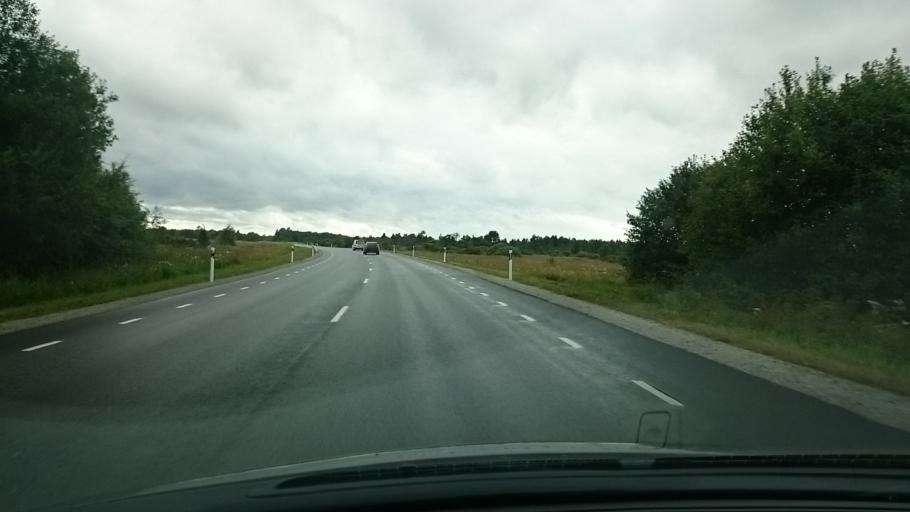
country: EE
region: Harju
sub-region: Keila linn
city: Keila
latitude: 59.3043
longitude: 24.3652
